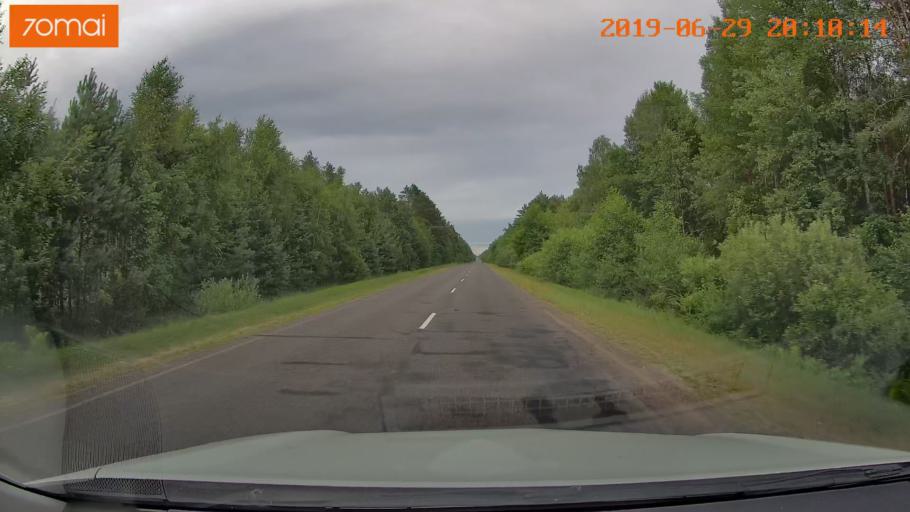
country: BY
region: Brest
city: Lahishyn
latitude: 52.3523
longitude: 26.0884
